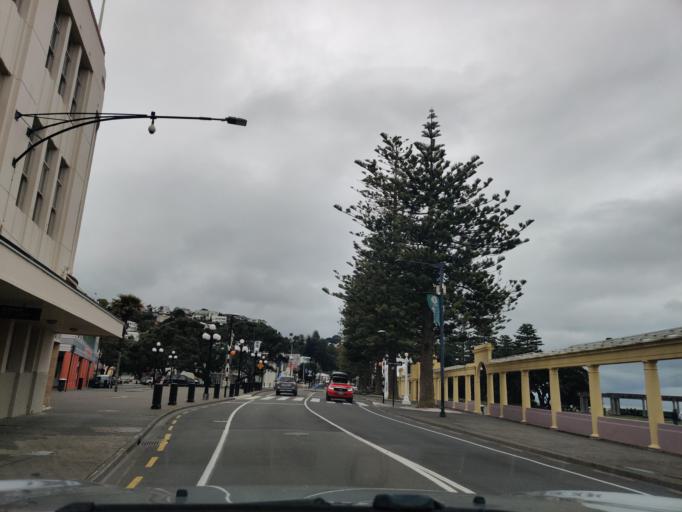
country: NZ
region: Hawke's Bay
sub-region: Napier City
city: Napier
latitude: -39.4902
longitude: 176.9193
